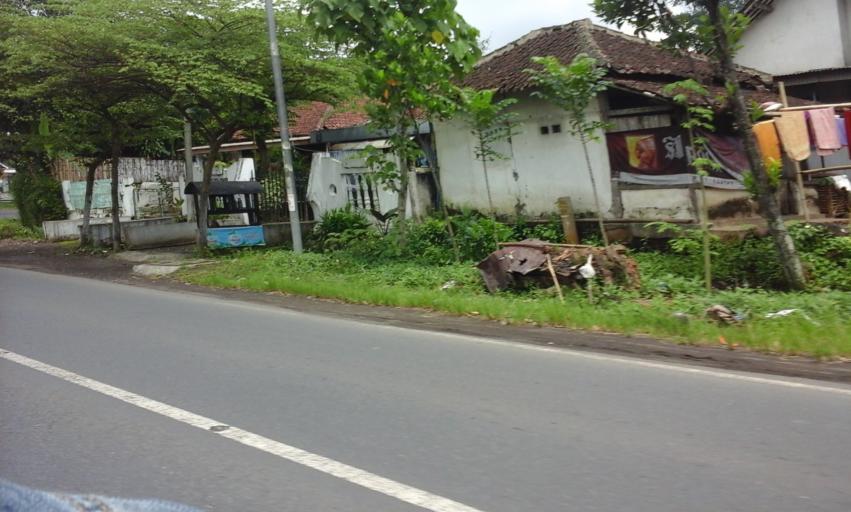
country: ID
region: East Java
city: Jatiroto
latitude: -8.1240
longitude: 113.3710
